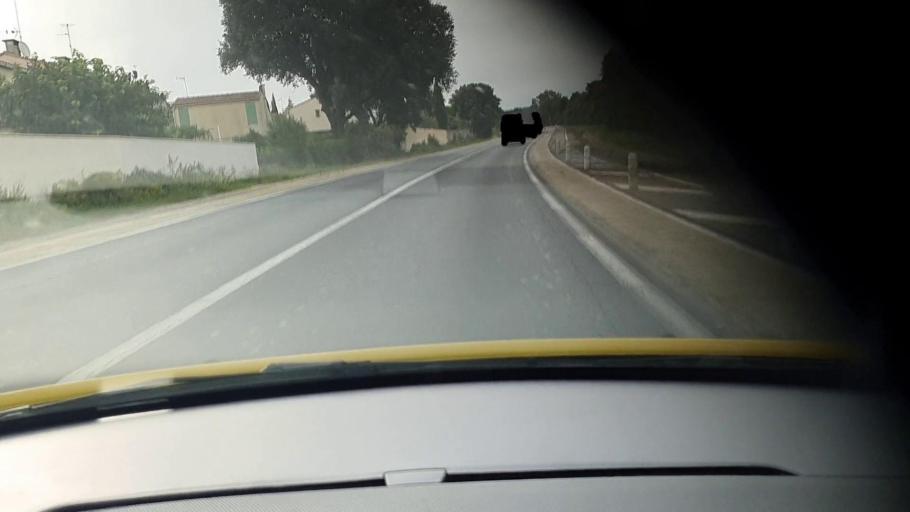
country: FR
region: Languedoc-Roussillon
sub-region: Departement du Gard
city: Caissargues
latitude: 43.7877
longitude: 4.3895
